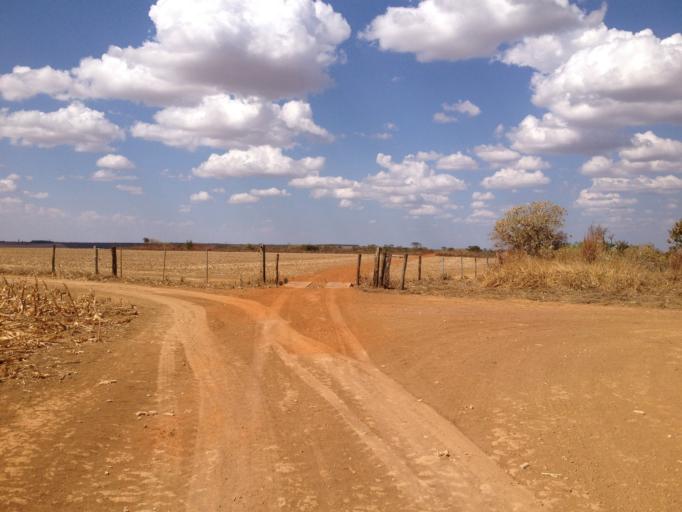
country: BR
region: Federal District
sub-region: Brasilia
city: Brasilia
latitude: -15.9027
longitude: -47.5925
